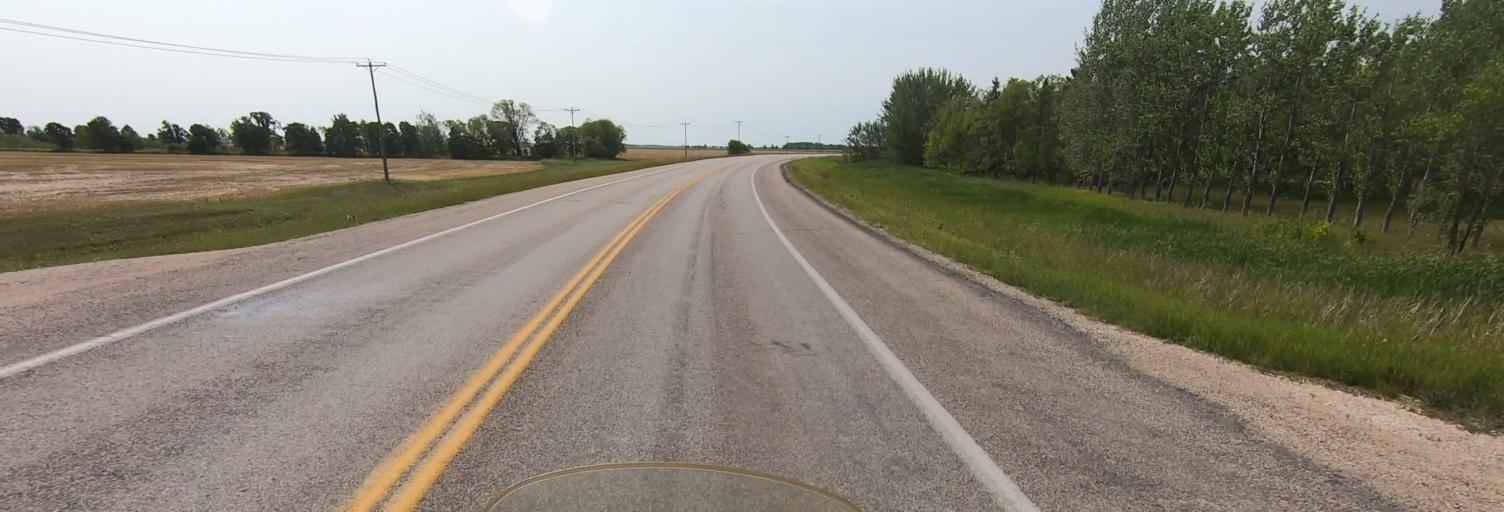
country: CA
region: Manitoba
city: Niverville
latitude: 49.6573
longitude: -97.1013
